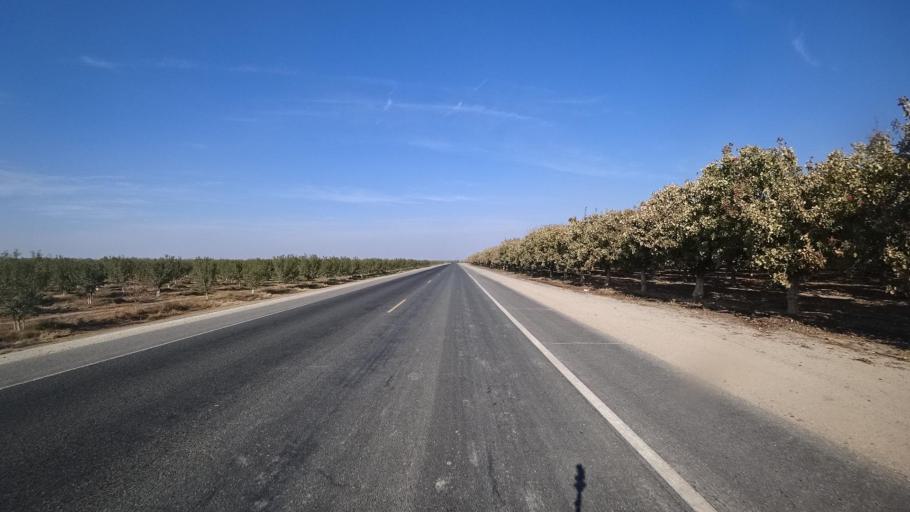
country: US
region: California
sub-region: Kern County
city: McFarland
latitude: 35.6529
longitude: -119.1957
